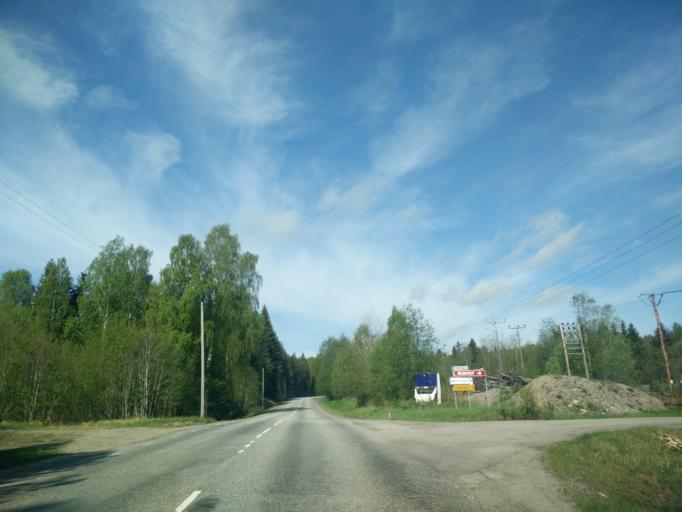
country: SE
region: Vaesternorrland
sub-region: Sundsvalls Kommun
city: Nolby
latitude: 62.2995
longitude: 17.3238
